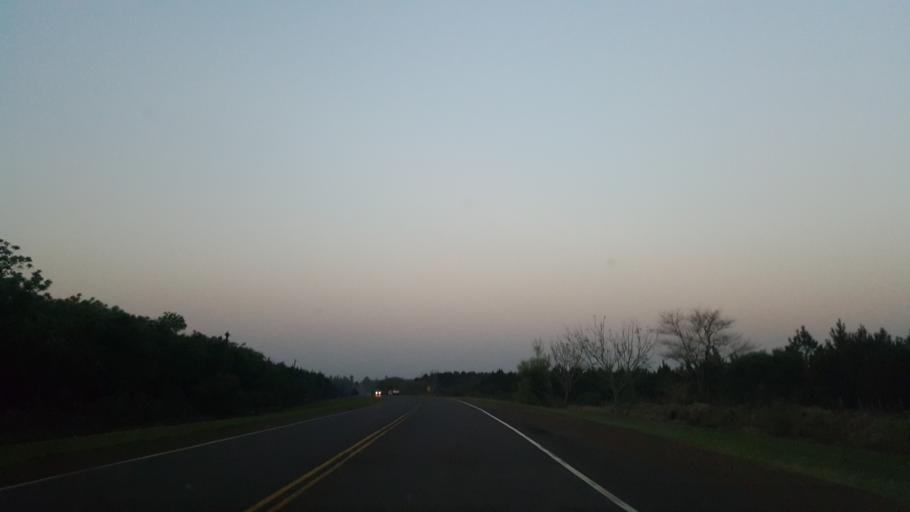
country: AR
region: Misiones
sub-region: Departamento de Capital
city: Posadas
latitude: -27.4359
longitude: -56.0140
